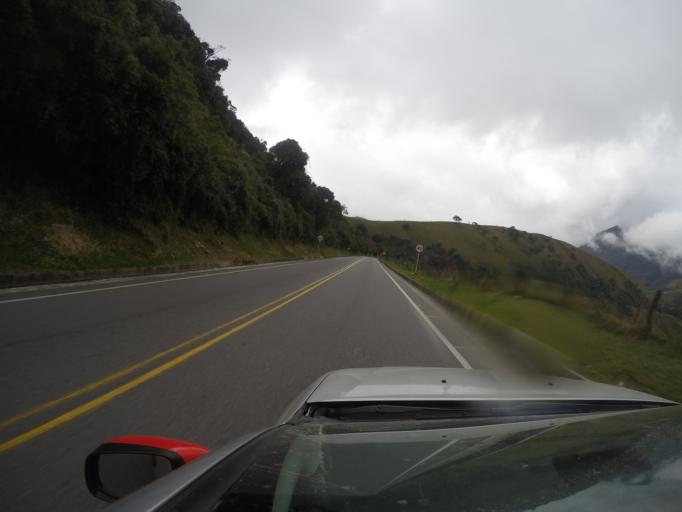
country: CO
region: Tolima
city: Herveo
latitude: 5.0619
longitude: -75.3123
